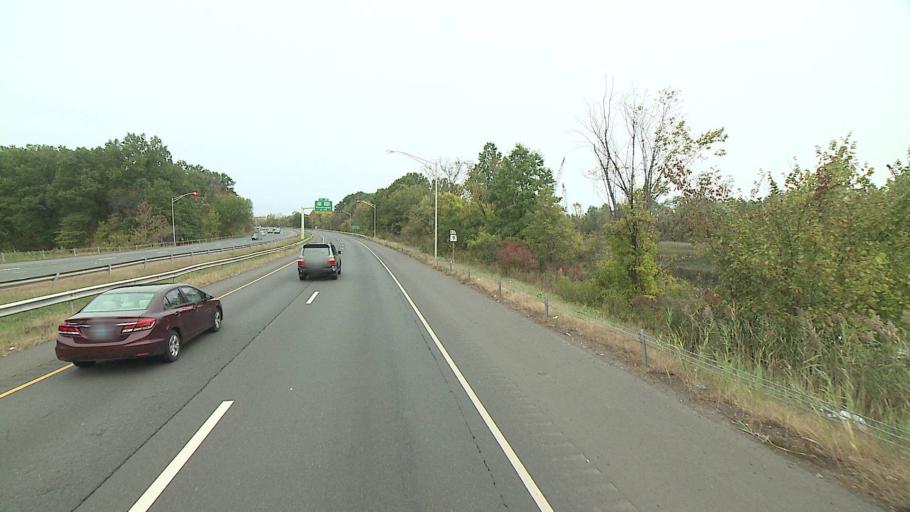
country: US
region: Connecticut
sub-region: Hartford County
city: Kensington
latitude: 41.6404
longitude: -72.7544
